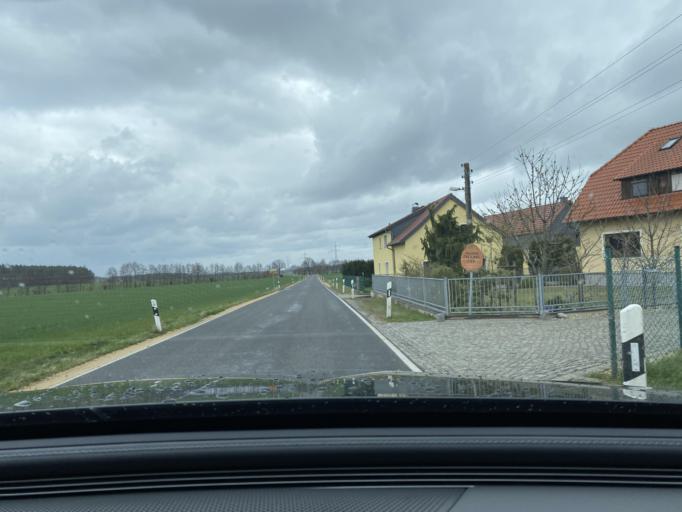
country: DE
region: Saxony
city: Grossdubrau
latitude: 51.2750
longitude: 14.4332
